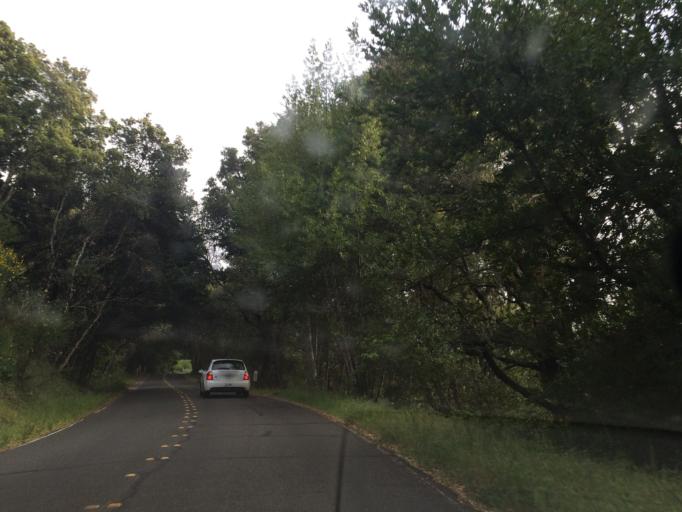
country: US
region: California
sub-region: Santa Clara County
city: Los Altos Hills
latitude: 37.3275
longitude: -122.1720
